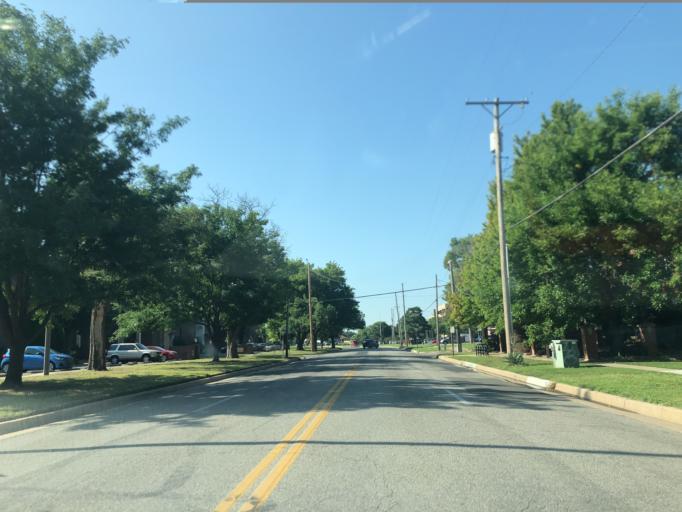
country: US
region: Kansas
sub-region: Sedgwick County
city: Wichita
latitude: 37.6997
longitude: -97.3420
